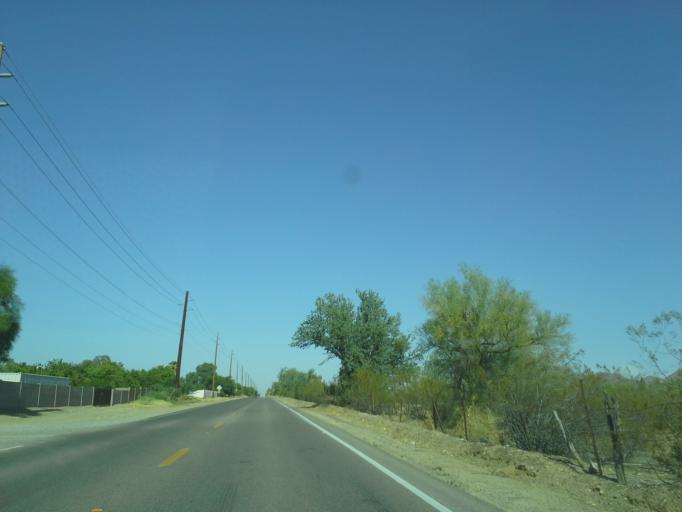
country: US
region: Arizona
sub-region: Maricopa County
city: Queen Creek
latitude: 33.2046
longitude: -111.6993
